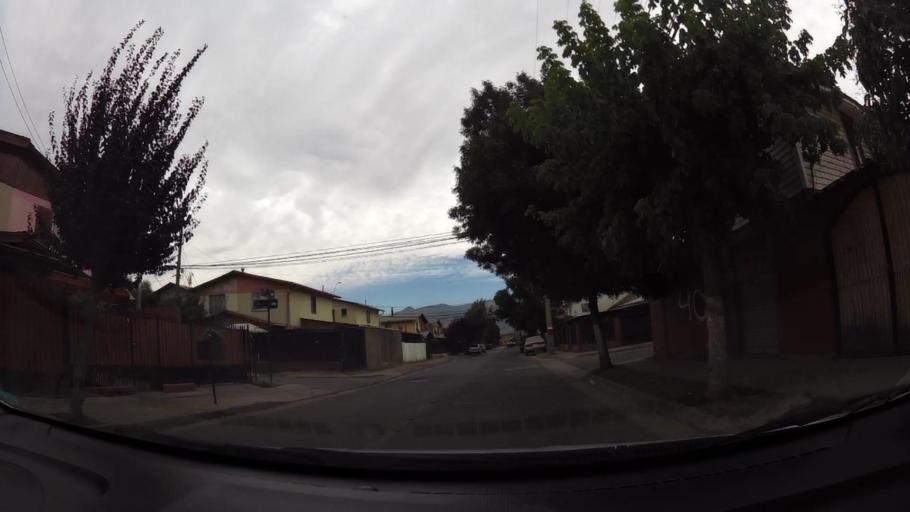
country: CL
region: O'Higgins
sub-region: Provincia de Cachapoal
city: Rancagua
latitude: -34.1257
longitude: -70.7366
